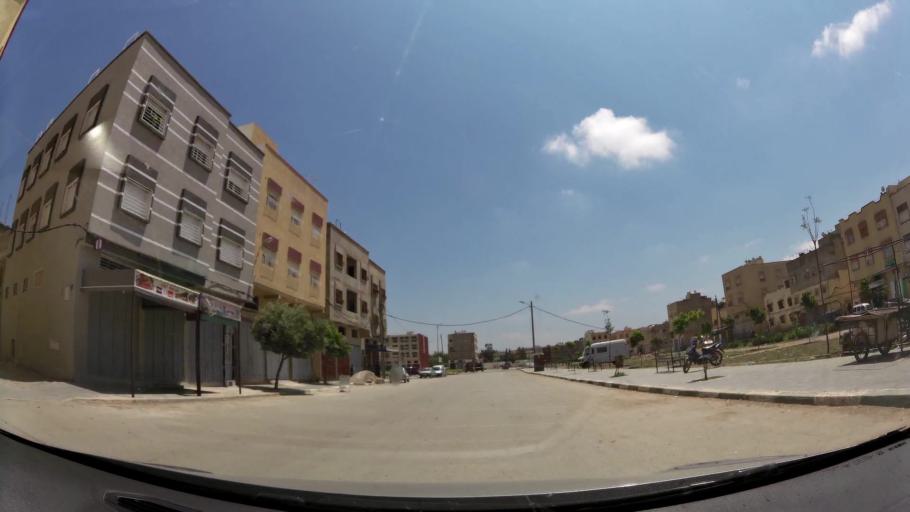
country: MA
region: Fes-Boulemane
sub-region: Fes
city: Fes
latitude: 34.0346
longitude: -5.0482
